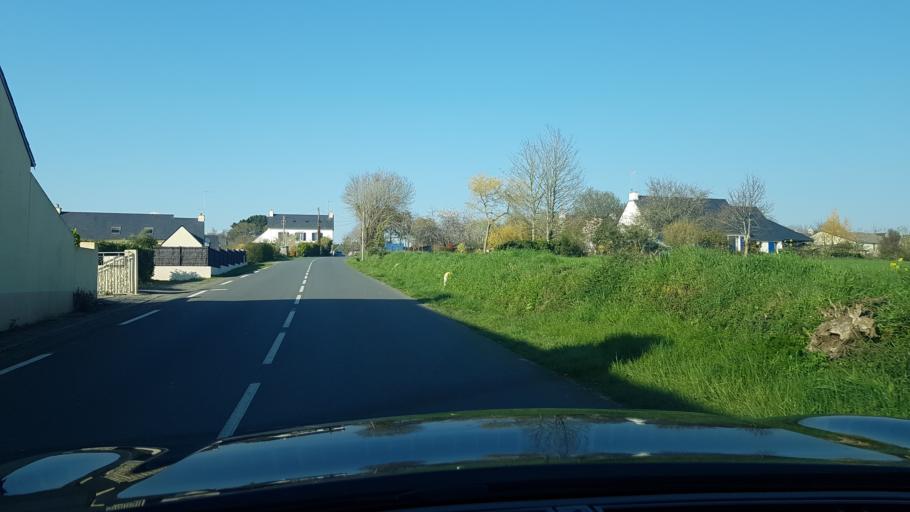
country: FR
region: Brittany
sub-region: Departement du Finistere
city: Clohars-Carnoet
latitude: 47.7772
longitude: -3.5941
